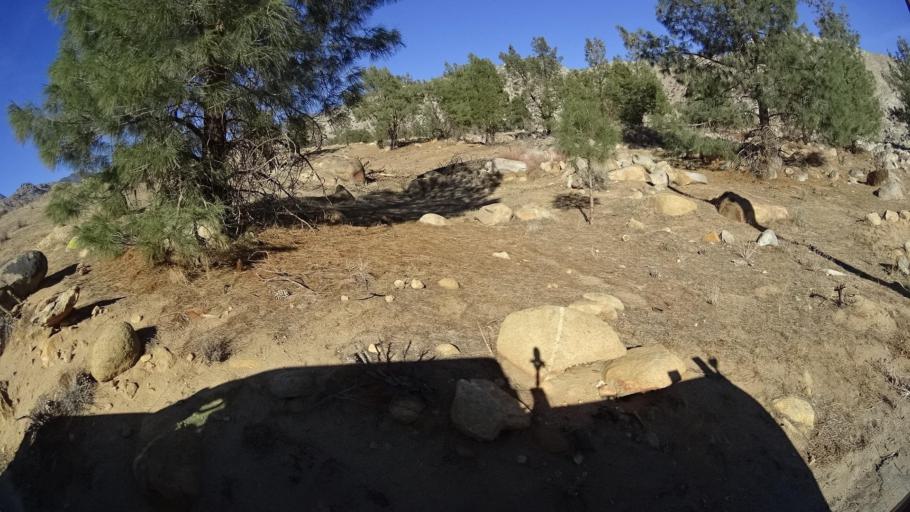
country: US
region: California
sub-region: Kern County
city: Weldon
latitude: 35.6965
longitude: -118.2983
